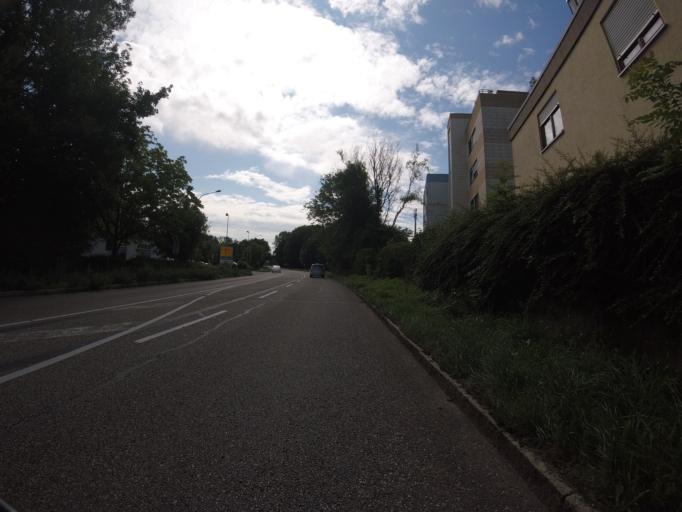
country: DE
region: Baden-Wuerttemberg
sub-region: Regierungsbezirk Stuttgart
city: Leutenbach
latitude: 48.8842
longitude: 9.3928
